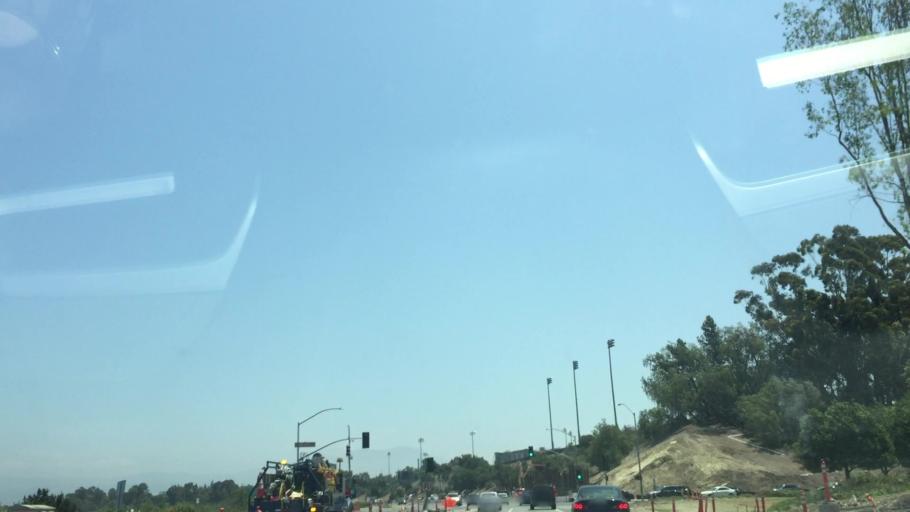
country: US
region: California
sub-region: Orange County
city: Irvine
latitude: 33.6506
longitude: -117.8545
